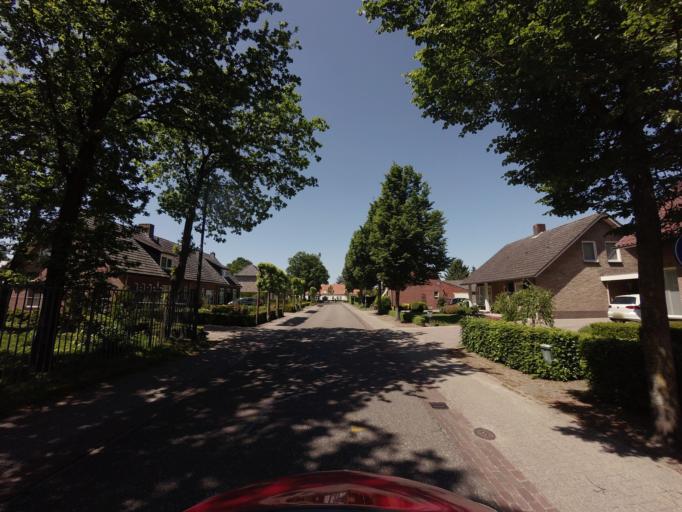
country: NL
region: North Brabant
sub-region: Gemeente Eersel
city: Eersel
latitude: 51.3076
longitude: 5.2949
